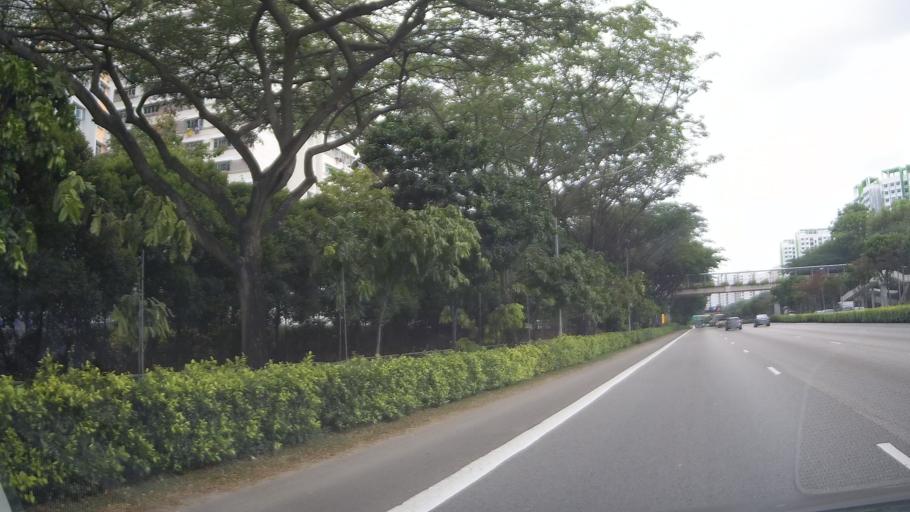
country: MY
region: Johor
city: Kampung Pasir Gudang Baru
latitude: 1.3904
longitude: 103.9102
